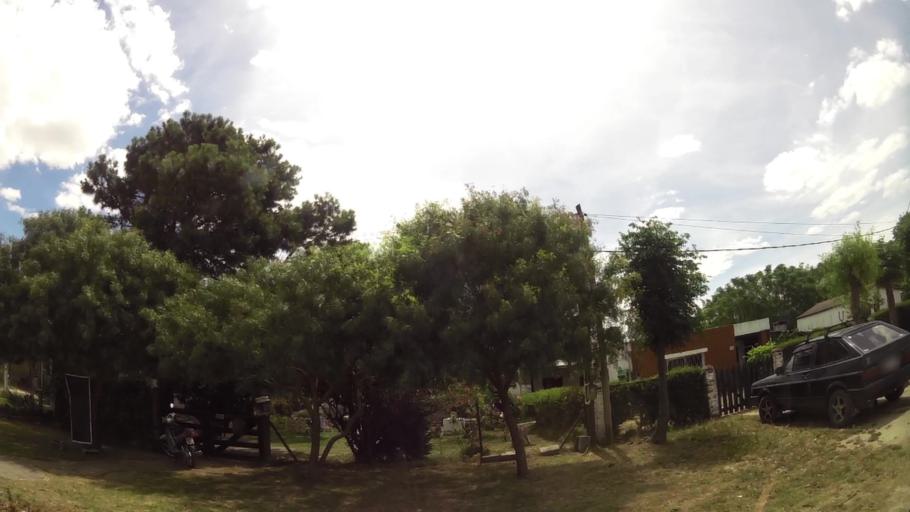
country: UY
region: San Jose
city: Delta del Tigre
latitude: -34.7501
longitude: -56.4562
